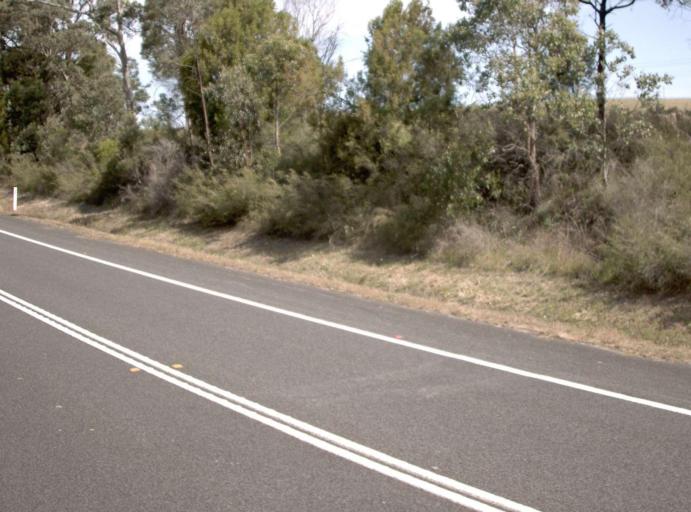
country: AU
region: Victoria
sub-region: East Gippsland
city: Lakes Entrance
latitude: -37.8274
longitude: 147.8970
